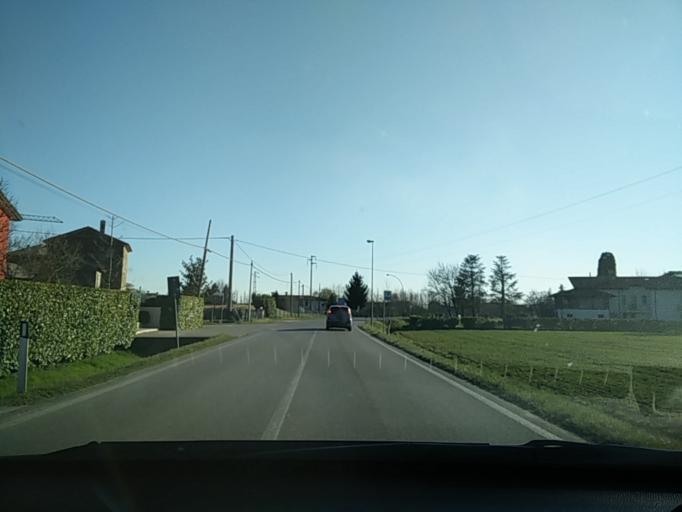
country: IT
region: Veneto
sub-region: Provincia di Treviso
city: Fontanelle
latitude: 45.8389
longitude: 12.4789
